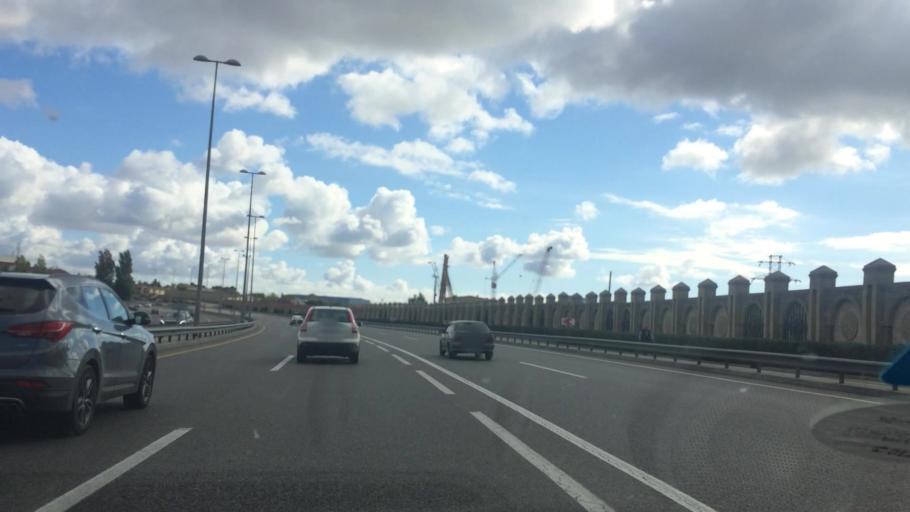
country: AZ
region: Baki
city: Ramana
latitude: 40.4384
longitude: 49.9770
